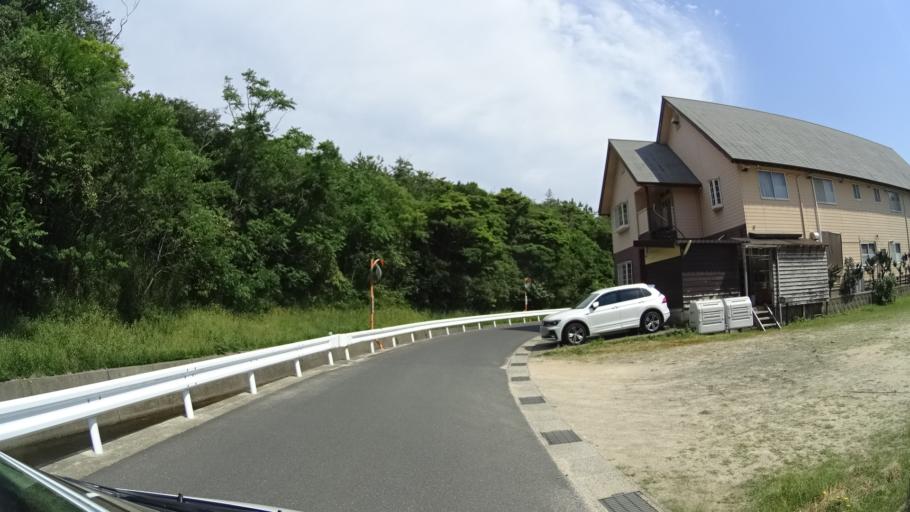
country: JP
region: Kyoto
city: Miyazu
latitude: 35.7015
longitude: 135.0541
